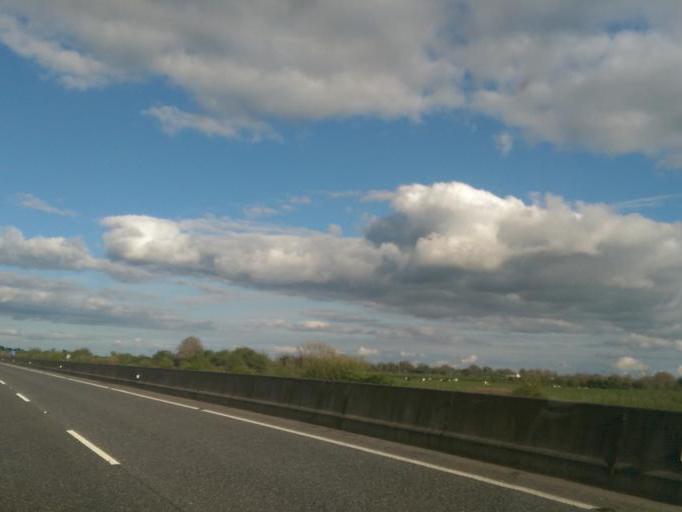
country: IE
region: Leinster
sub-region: An Iarmhi
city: Kinnegad
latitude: 53.4494
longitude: -7.1644
